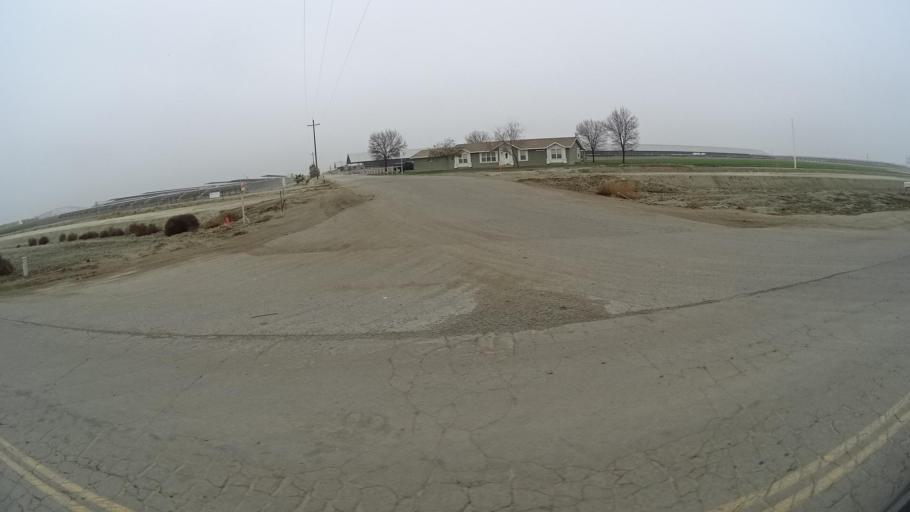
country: US
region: California
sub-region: Kern County
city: Rosedale
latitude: 35.2096
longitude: -119.2133
